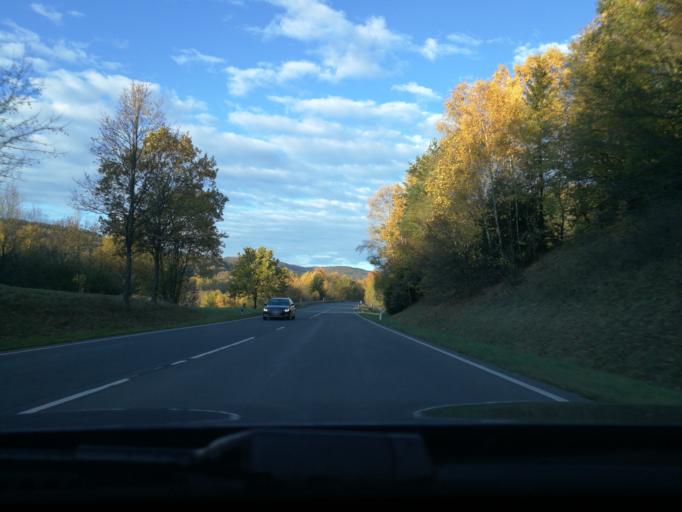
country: DE
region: Bavaria
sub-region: Regierungsbezirk Unterfranken
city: Wildflecken
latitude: 50.3659
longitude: 9.8967
